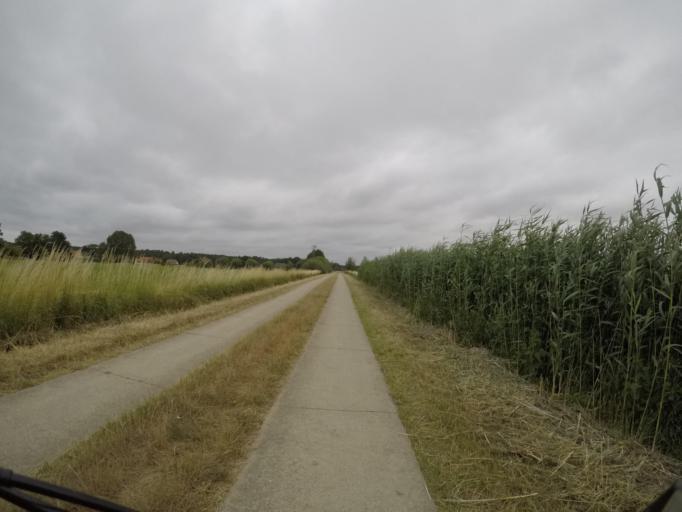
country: DE
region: Lower Saxony
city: Hitzacker
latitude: 53.1771
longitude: 11.0828
